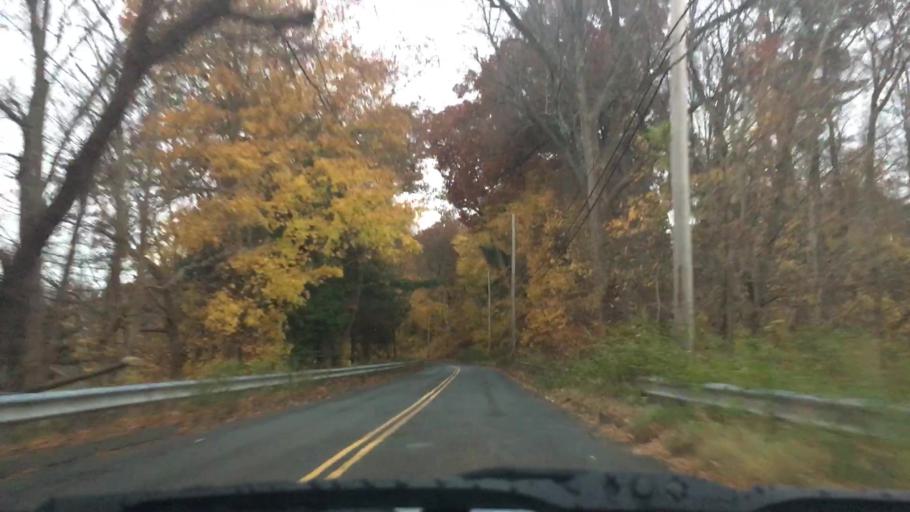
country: US
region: Massachusetts
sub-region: Hampden County
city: Westfield
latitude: 42.1269
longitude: -72.7774
